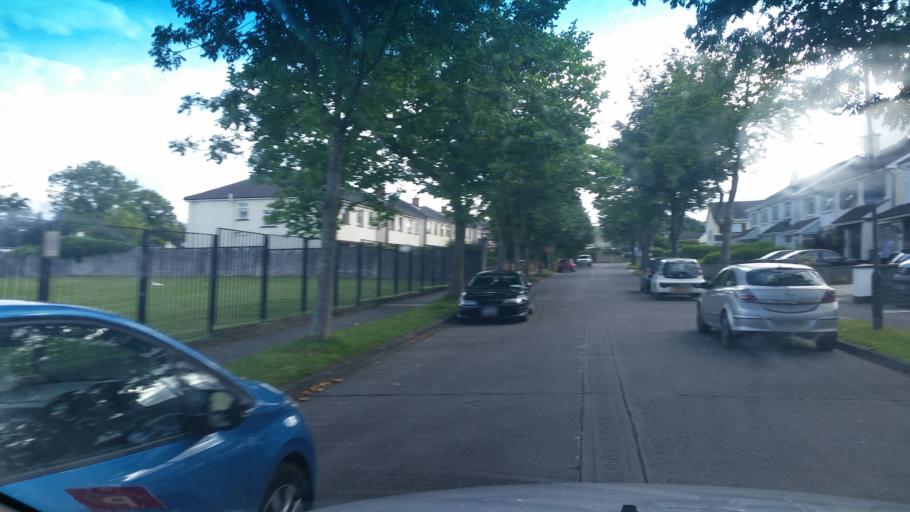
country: IE
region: Leinster
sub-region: Fingal County
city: Blanchardstown
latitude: 53.3848
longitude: -6.3830
